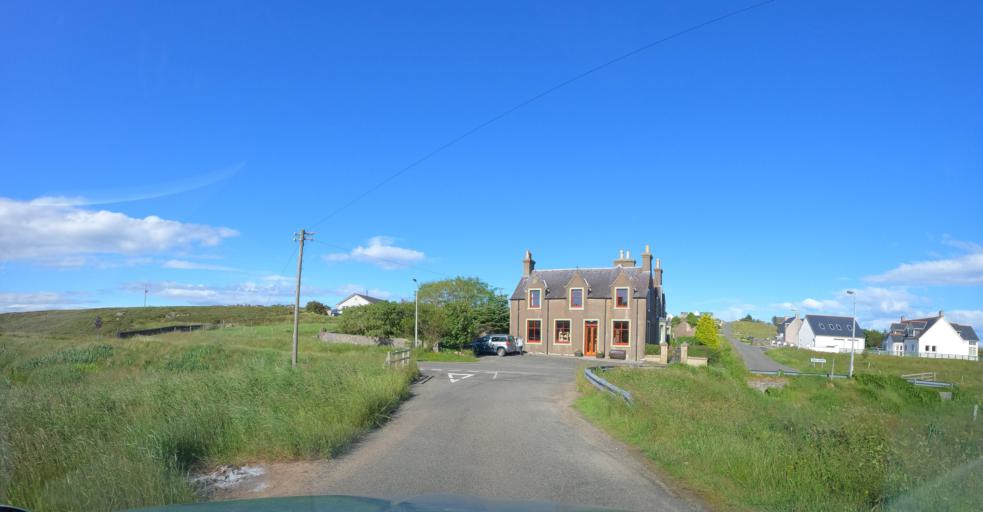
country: GB
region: Scotland
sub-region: Eilean Siar
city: Stornoway
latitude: 58.2040
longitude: -6.2153
